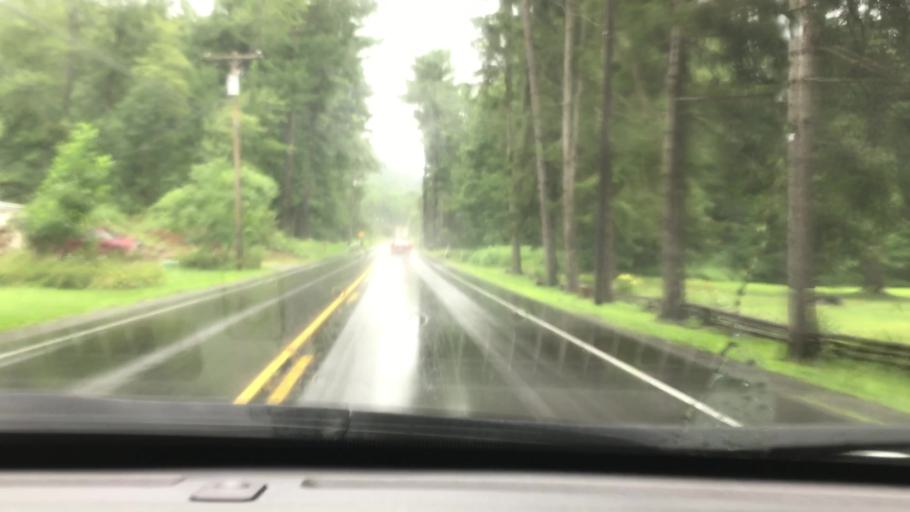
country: US
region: Pennsylvania
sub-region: Blair County
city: Tyrone
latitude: 40.7496
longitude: -78.2141
